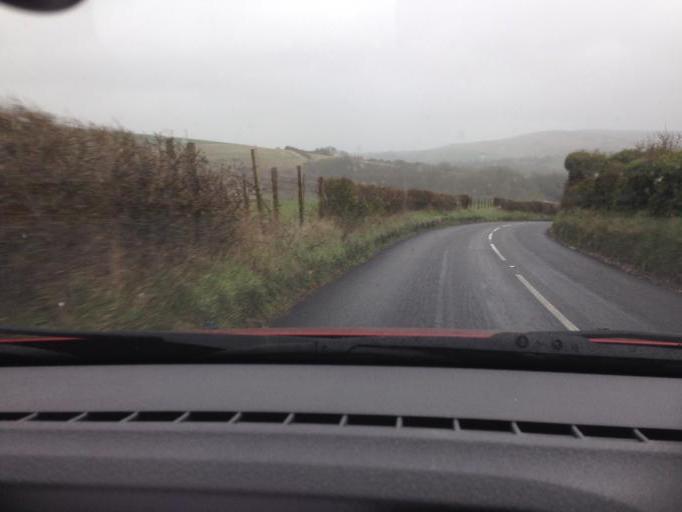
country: GB
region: England
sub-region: East Sussex
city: Seaford
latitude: 50.7930
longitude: 0.1443
